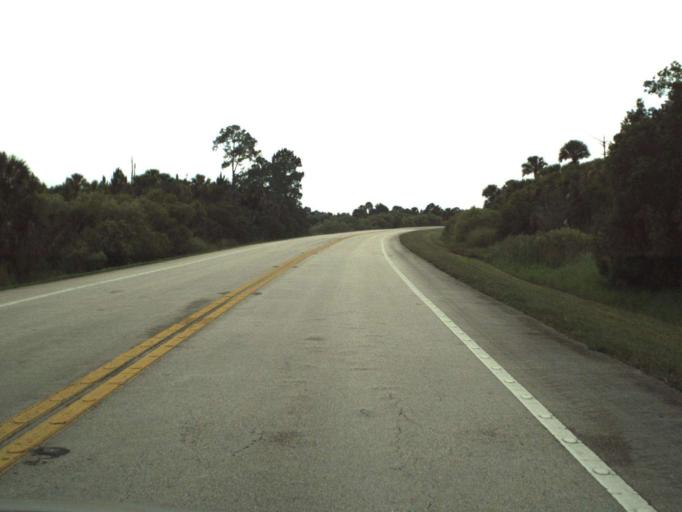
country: US
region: Florida
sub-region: Brevard County
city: Mims
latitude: 28.6654
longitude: -80.9597
